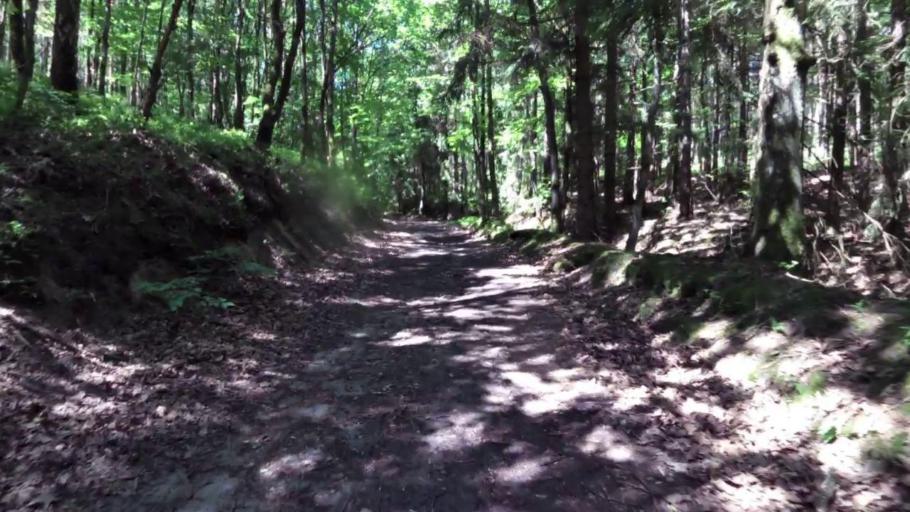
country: PL
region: West Pomeranian Voivodeship
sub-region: Powiat bialogardzki
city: Bialogard
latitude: 53.9590
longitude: 16.0893
